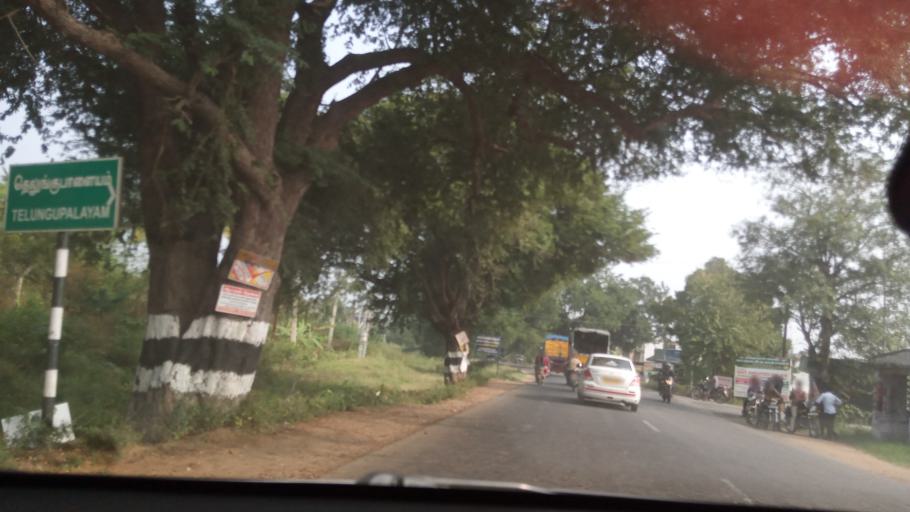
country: IN
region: Tamil Nadu
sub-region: Coimbatore
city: Annur
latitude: 11.1867
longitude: 77.0632
